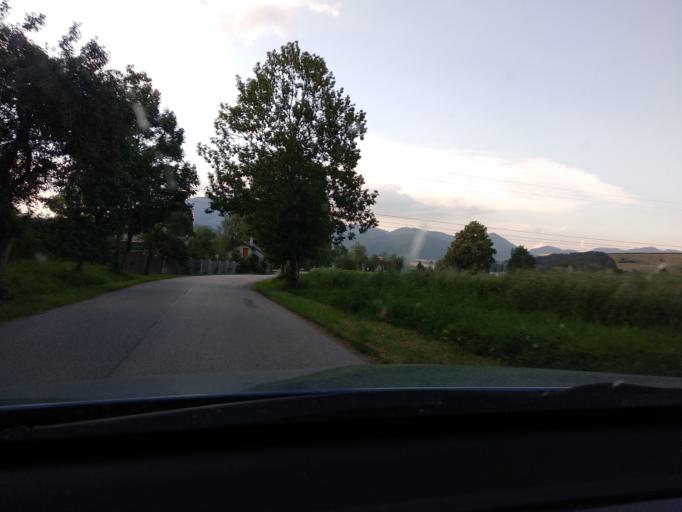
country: SK
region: Zilinsky
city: Ruzomberok
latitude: 49.0606
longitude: 19.3359
